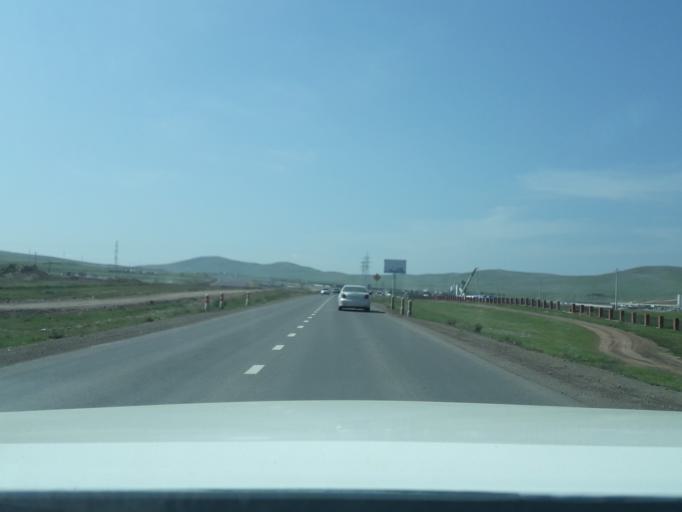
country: MN
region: Ulaanbaatar
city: Ulaanbaatar
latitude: 47.8232
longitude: 106.7641
